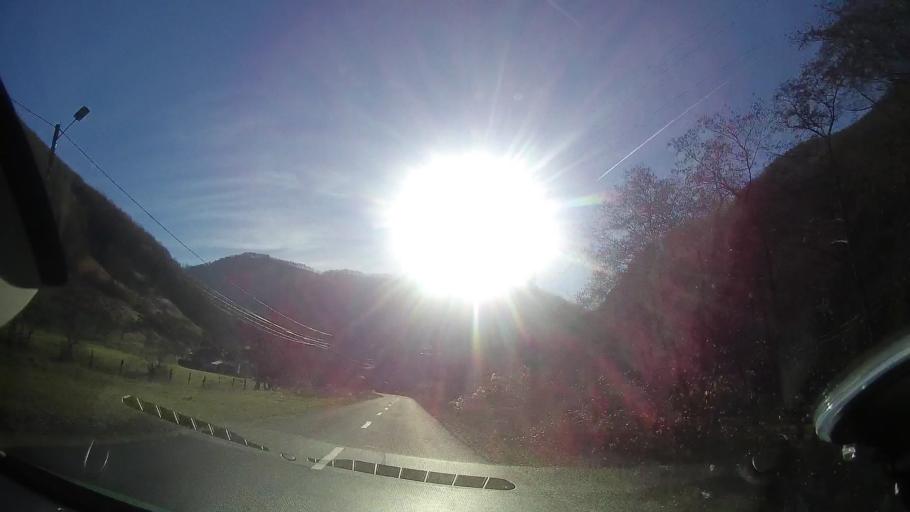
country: RO
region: Bihor
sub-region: Comuna Bulz
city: Bulz
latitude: 46.9206
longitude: 22.6542
